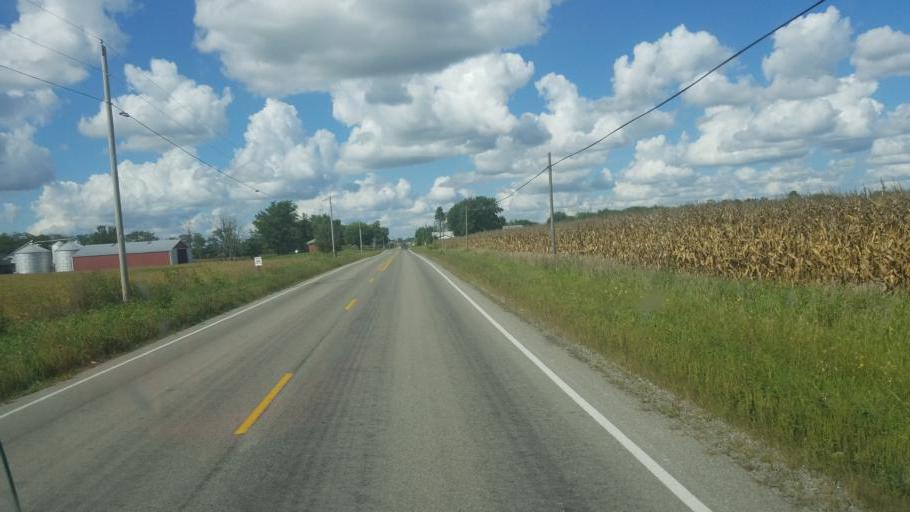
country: US
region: Ohio
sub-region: Hardin County
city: Kenton
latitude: 40.5198
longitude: -83.5741
